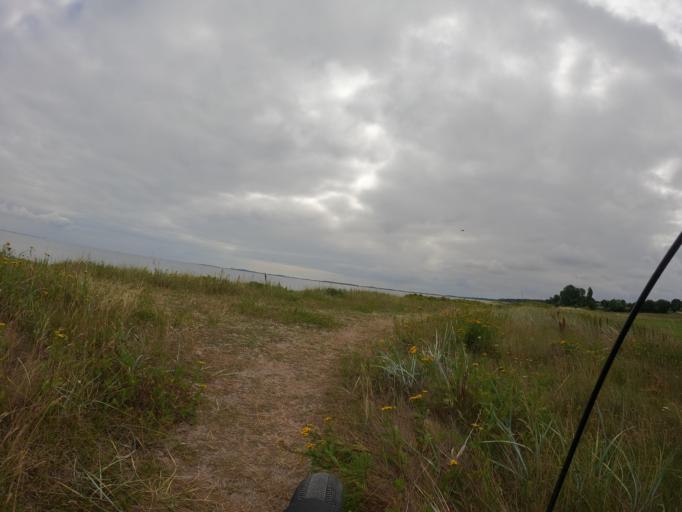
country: DE
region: Schleswig-Holstein
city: Steinberg
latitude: 54.7912
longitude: 9.7955
